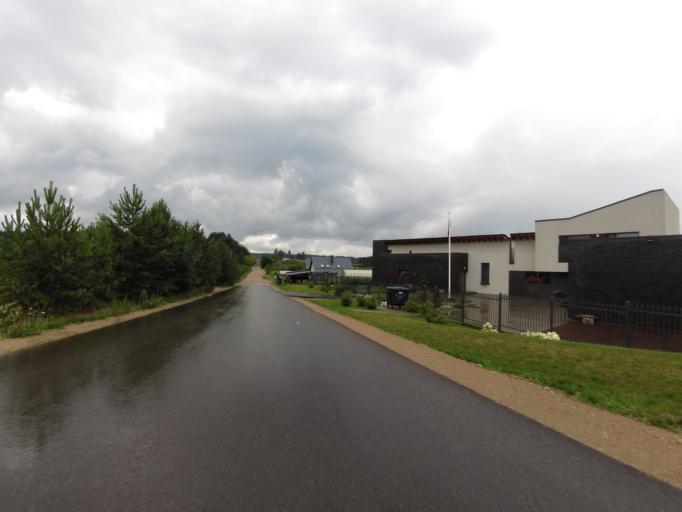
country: LT
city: Grigiskes
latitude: 54.7123
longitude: 25.1294
